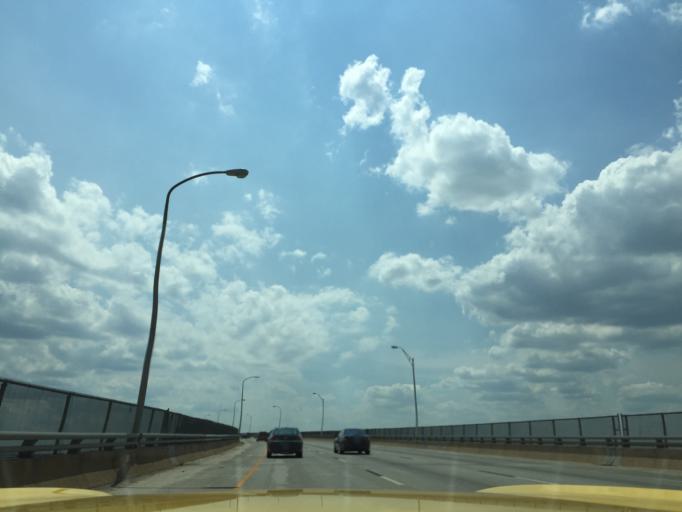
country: US
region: New Jersey
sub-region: Gloucester County
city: National Park
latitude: 39.8961
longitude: -75.1919
